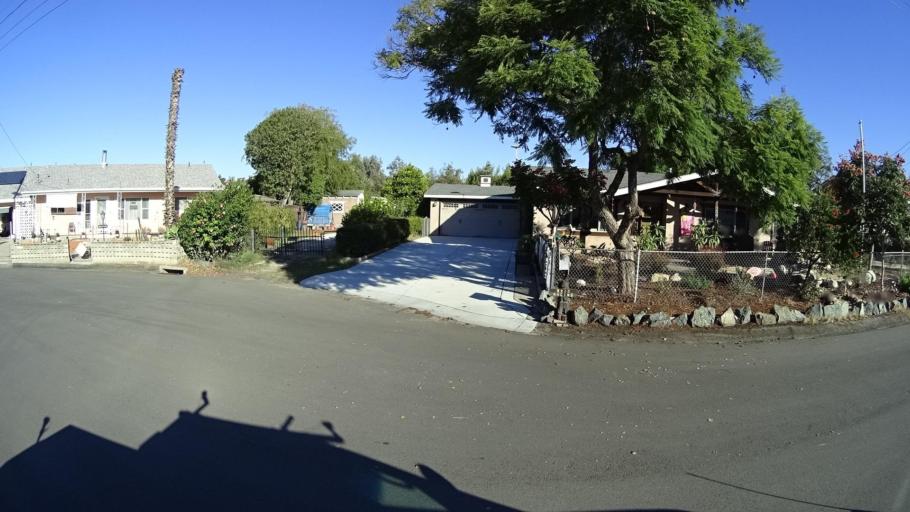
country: US
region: California
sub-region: San Diego County
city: Bonita
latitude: 32.6818
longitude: -117.0222
